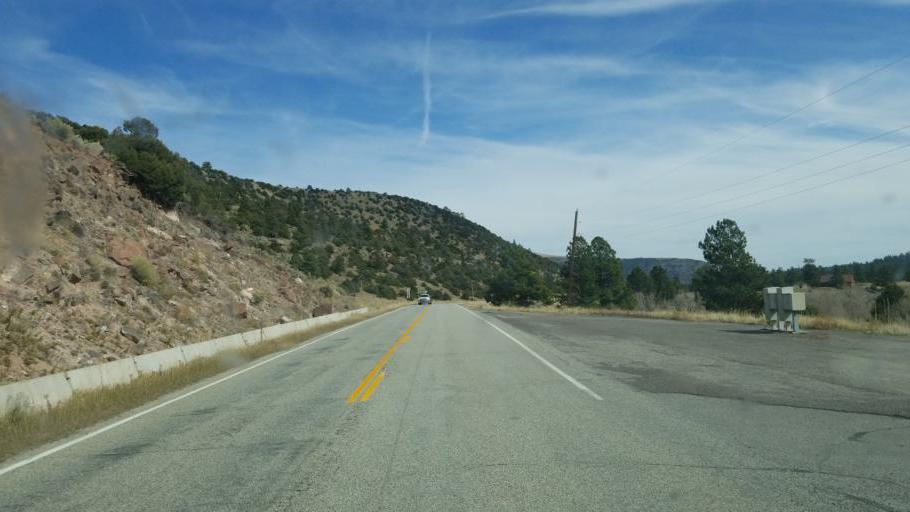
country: US
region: Colorado
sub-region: Conejos County
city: Conejos
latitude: 37.0688
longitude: -106.2448
